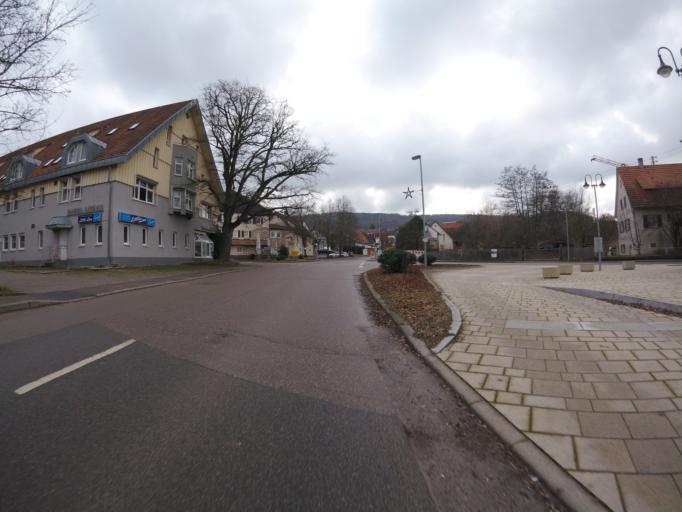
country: DE
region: Baden-Wuerttemberg
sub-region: Regierungsbezirk Stuttgart
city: Allmersbach im Tal
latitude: 48.9085
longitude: 9.4851
